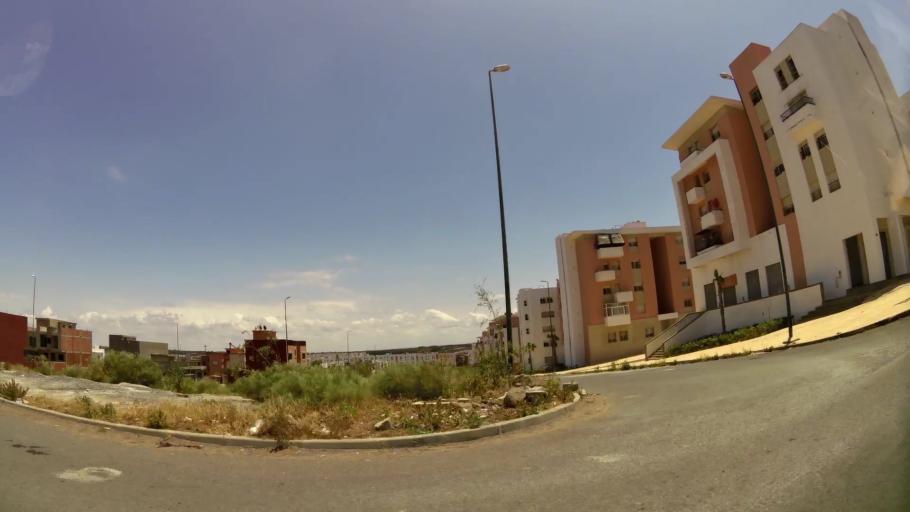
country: MA
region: Gharb-Chrarda-Beni Hssen
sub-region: Kenitra Province
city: Kenitra
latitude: 34.2542
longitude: -6.6574
